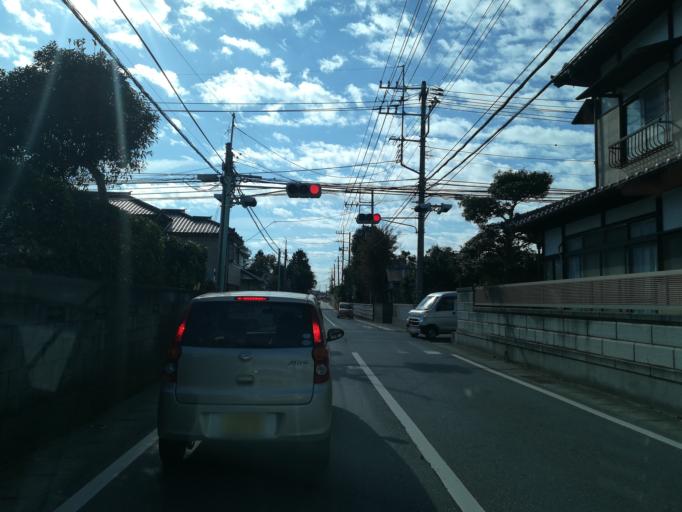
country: JP
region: Ibaraki
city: Naka
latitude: 36.0788
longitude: 140.1002
